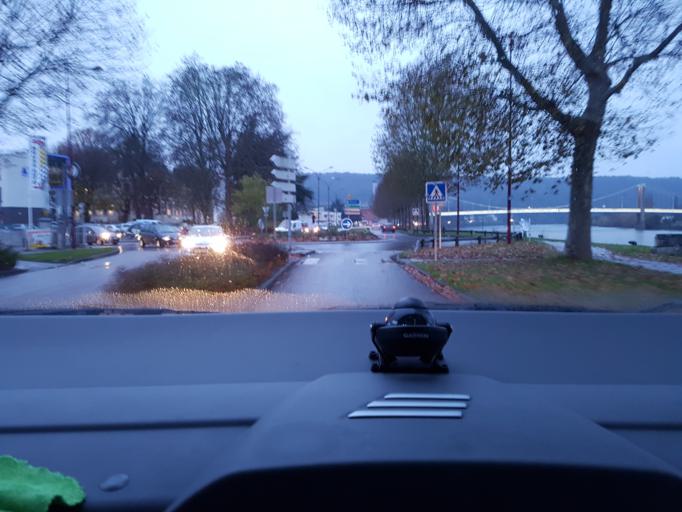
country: FR
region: Haute-Normandie
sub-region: Departement de la Seine-Maritime
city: Elbeuf
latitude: 49.2927
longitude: 1.0097
